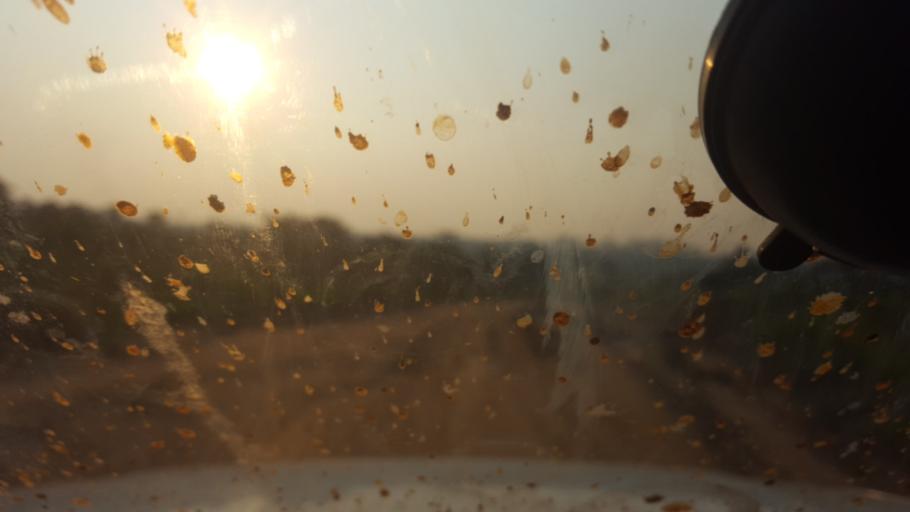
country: CD
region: Bandundu
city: Mushie
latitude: -3.7504
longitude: 16.6631
